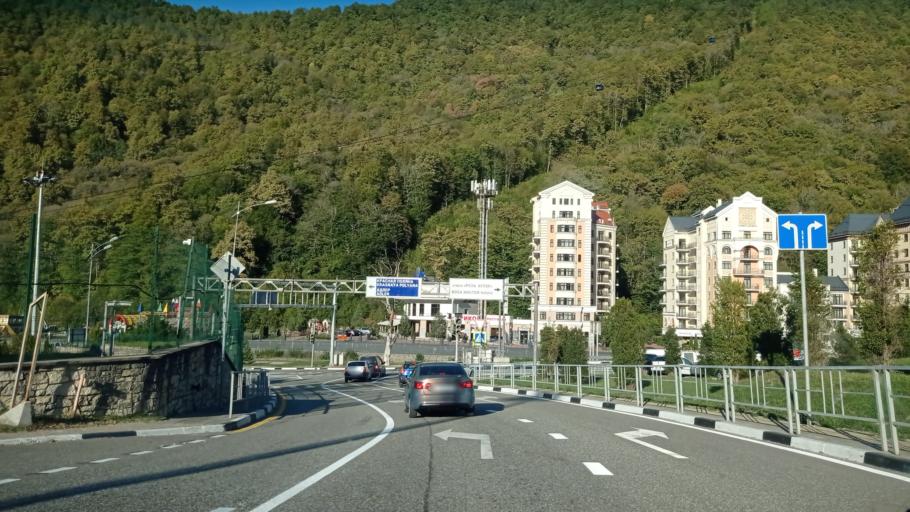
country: RU
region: Krasnodarskiy
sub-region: Sochi City
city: Krasnaya Polyana
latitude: 43.6750
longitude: 40.2846
